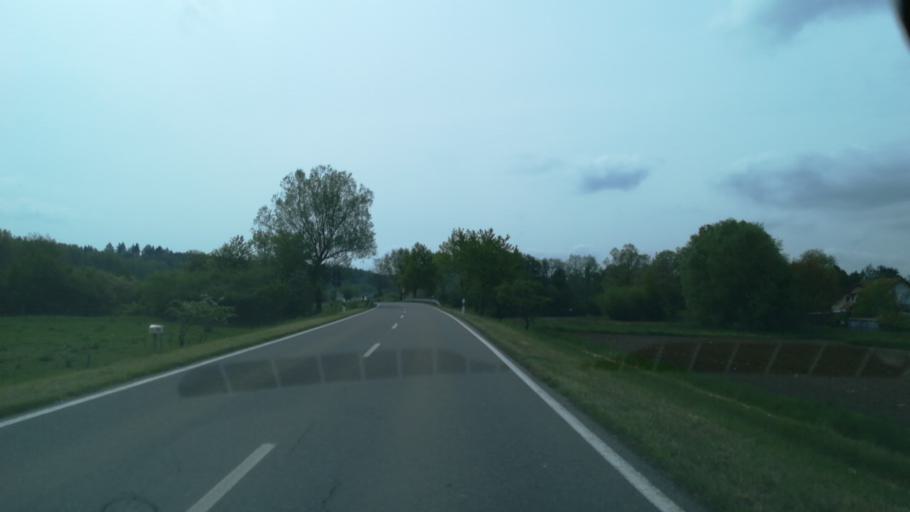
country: DE
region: Baden-Wuerttemberg
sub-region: Freiburg Region
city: Volkertshausen
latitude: 47.8045
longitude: 8.8776
